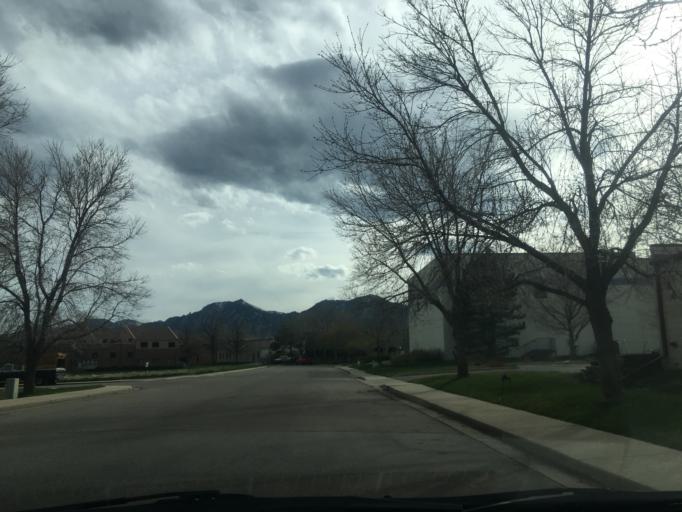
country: US
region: Colorado
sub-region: Boulder County
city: Boulder
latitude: 40.0323
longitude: -105.2272
